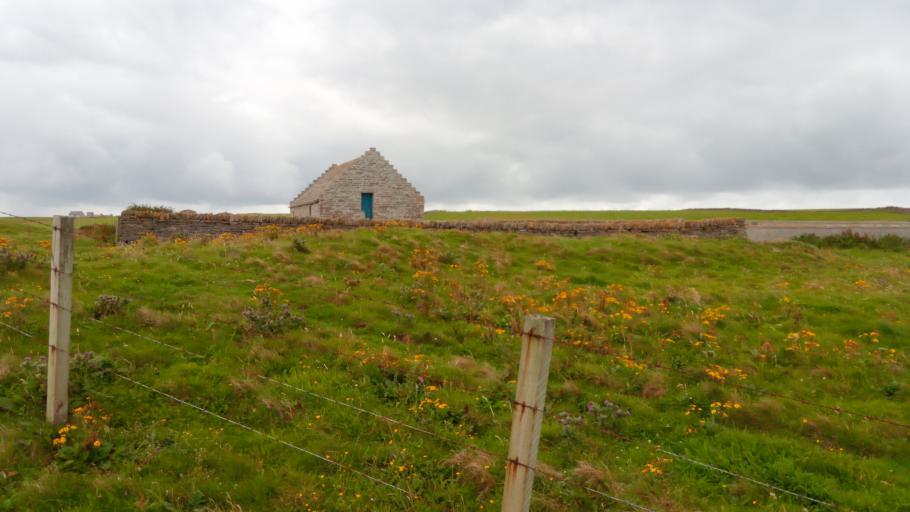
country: GB
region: Scotland
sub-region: Orkney Islands
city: Kirkwall
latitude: 59.3578
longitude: -2.9022
